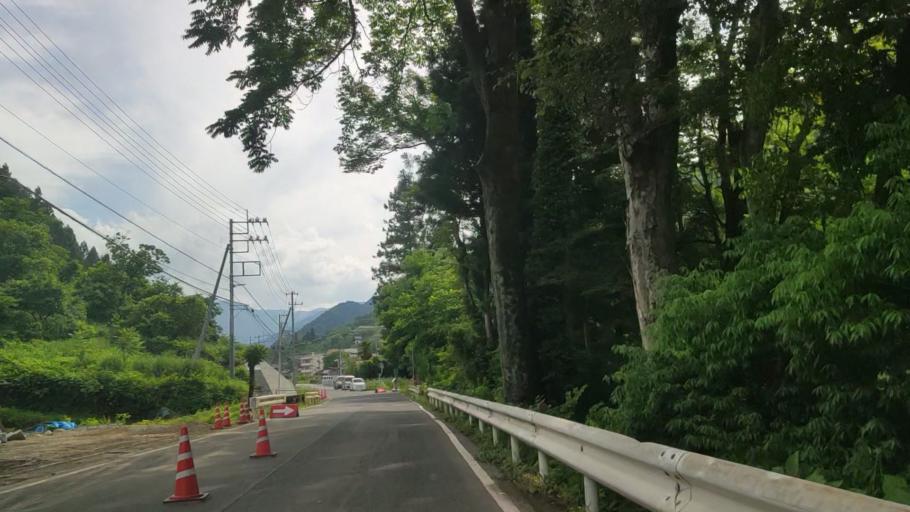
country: JP
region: Gunma
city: Tomioka
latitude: 36.1769
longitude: 138.7391
